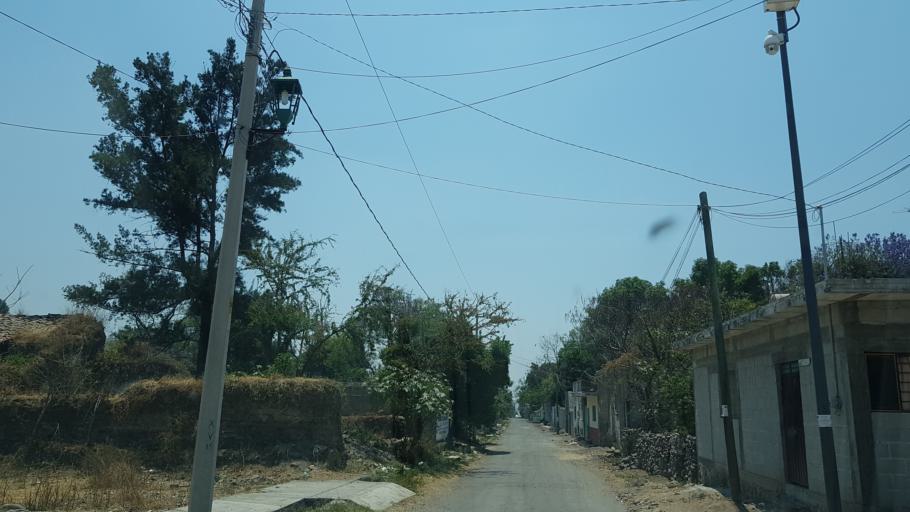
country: MX
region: Puebla
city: Huaquechula
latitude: 18.7771
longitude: -98.5449
